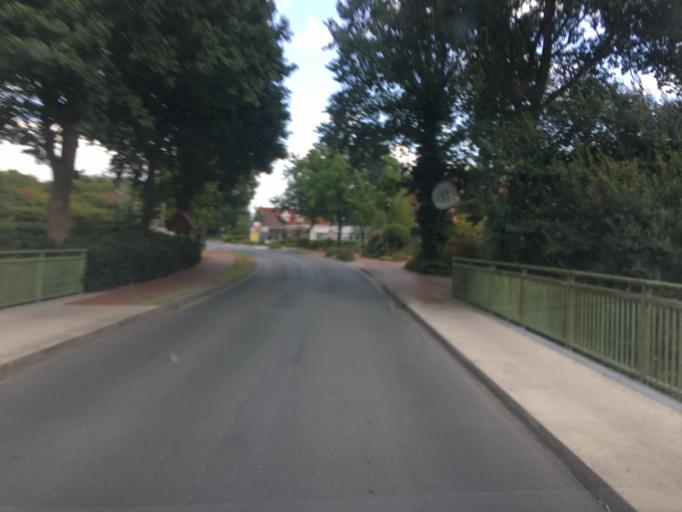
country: DE
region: Lower Saxony
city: Hilkenbrook
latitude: 53.0722
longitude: 7.6992
